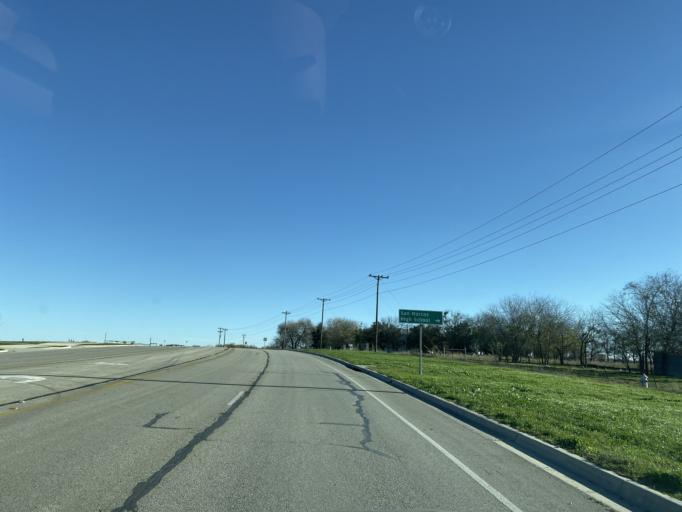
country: US
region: Texas
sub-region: Guadalupe County
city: Redwood
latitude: 29.8290
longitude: -97.9602
